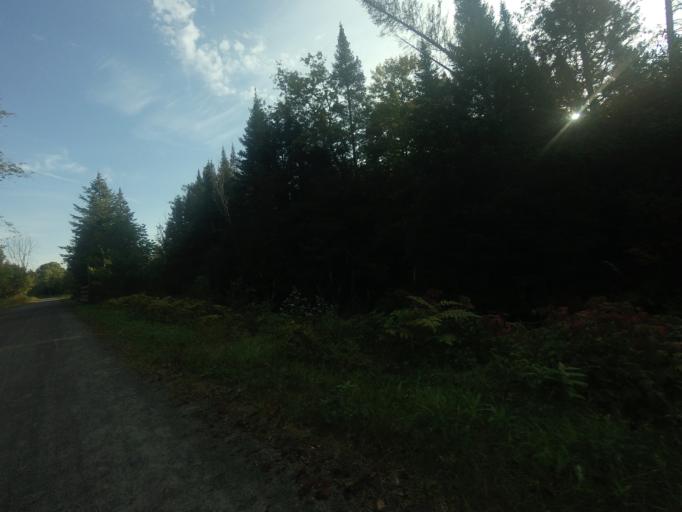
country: CA
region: Quebec
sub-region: Laurentides
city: Sainte-Adele
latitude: 45.9519
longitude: -74.1129
